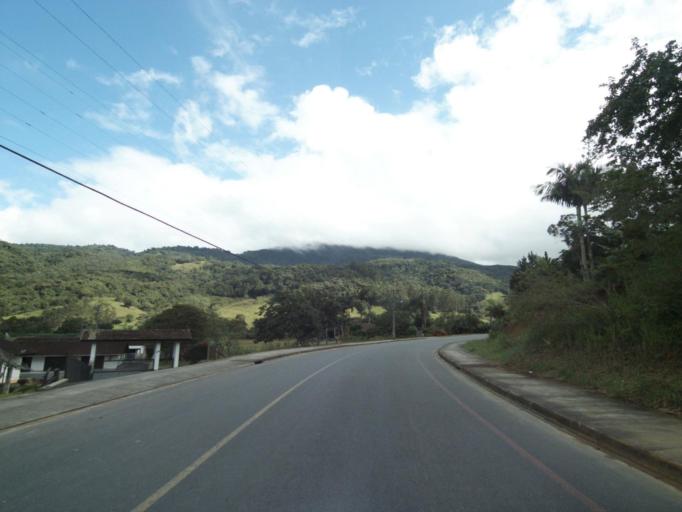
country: BR
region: Santa Catarina
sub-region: Pomerode
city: Pomerode
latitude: -26.6781
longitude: -49.1822
